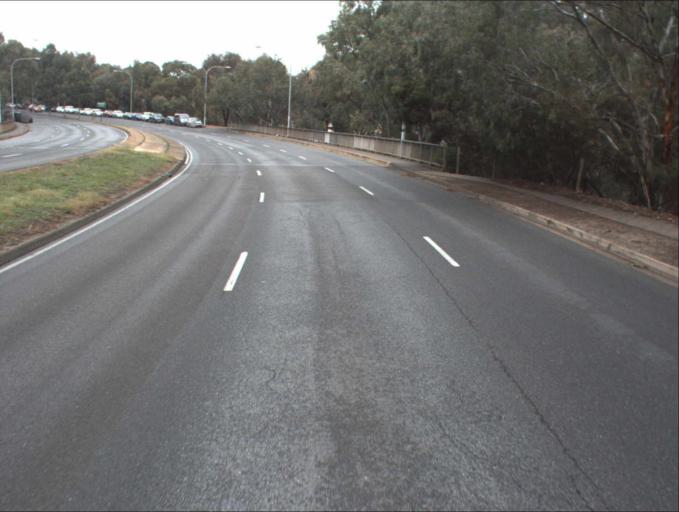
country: AU
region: South Australia
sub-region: Campbelltown
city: Paradise
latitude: -34.8643
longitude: 138.6613
